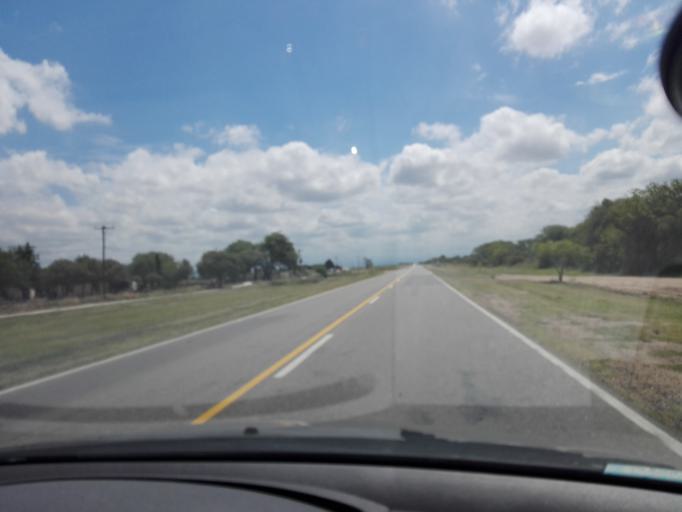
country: AR
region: Cordoba
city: Toledo
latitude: -31.6482
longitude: -64.1028
